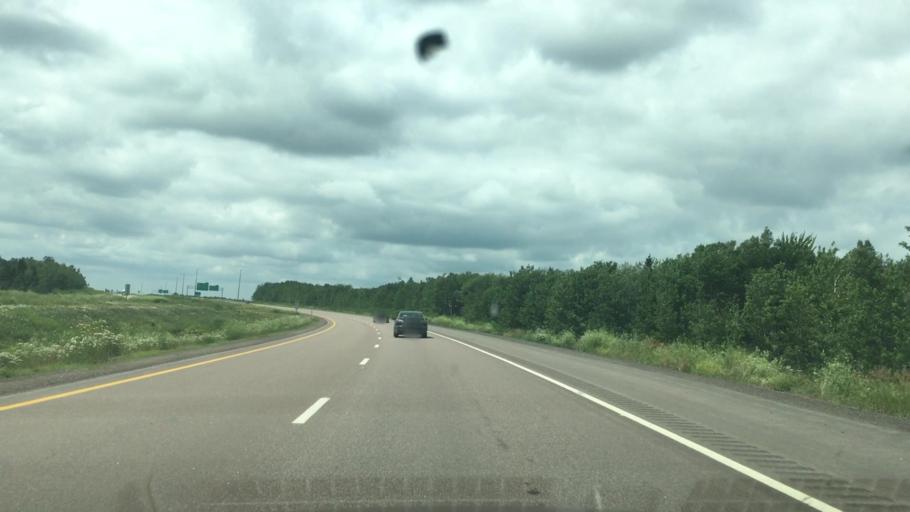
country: CA
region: New Brunswick
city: Dieppe
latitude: 46.1304
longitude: -64.6621
